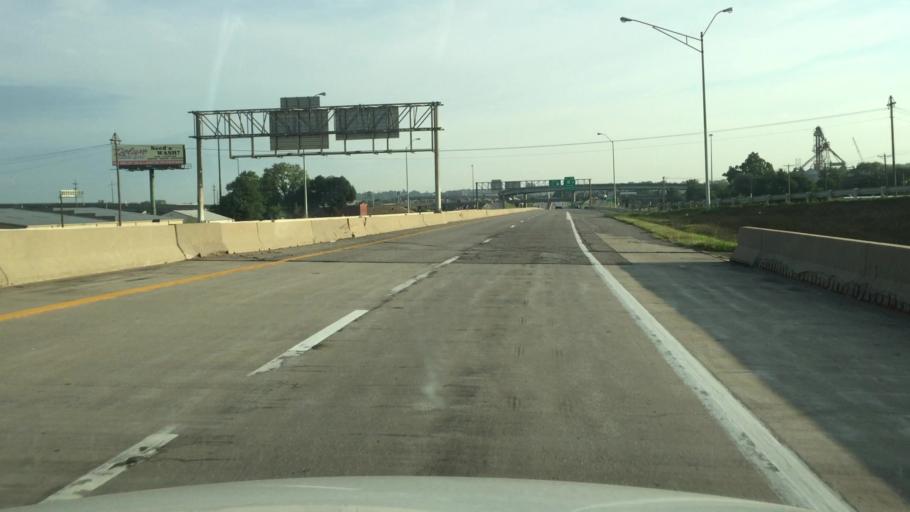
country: US
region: Kansas
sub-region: Doniphan County
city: Elwood
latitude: 39.7434
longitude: -94.8535
